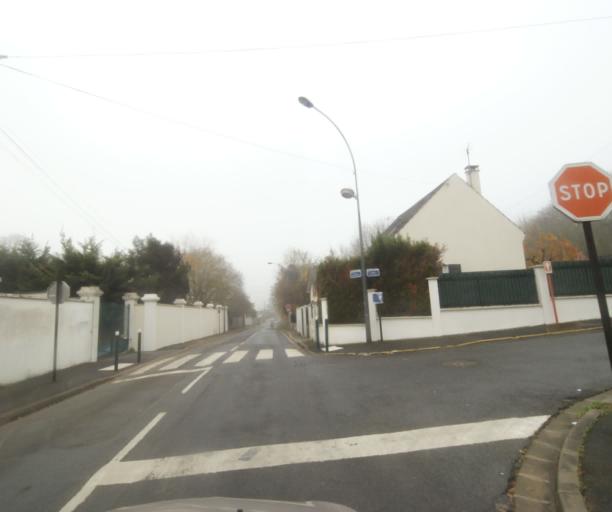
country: FR
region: Ile-de-France
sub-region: Departement de Seine-Saint-Denis
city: Vaujours
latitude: 48.9307
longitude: 2.5712
